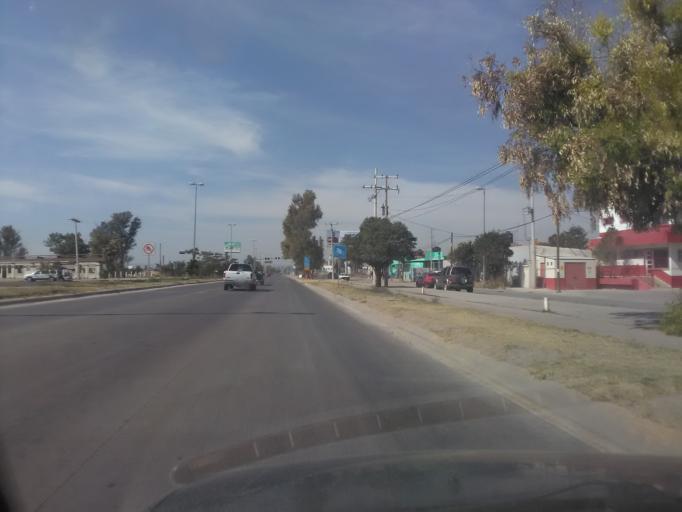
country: MX
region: Durango
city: Victoria de Durango
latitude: 24.0738
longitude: -104.5942
